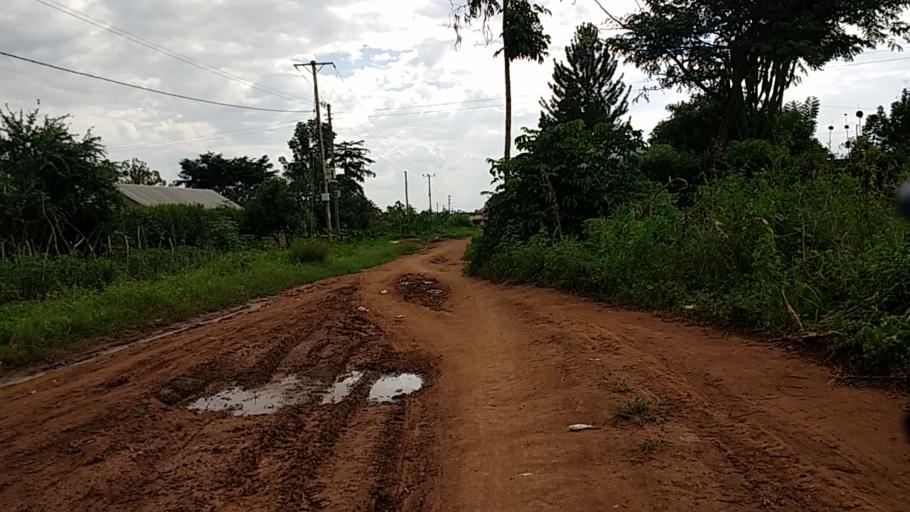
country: UG
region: Eastern Region
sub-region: Mbale District
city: Mbale
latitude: 1.0669
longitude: 34.1660
